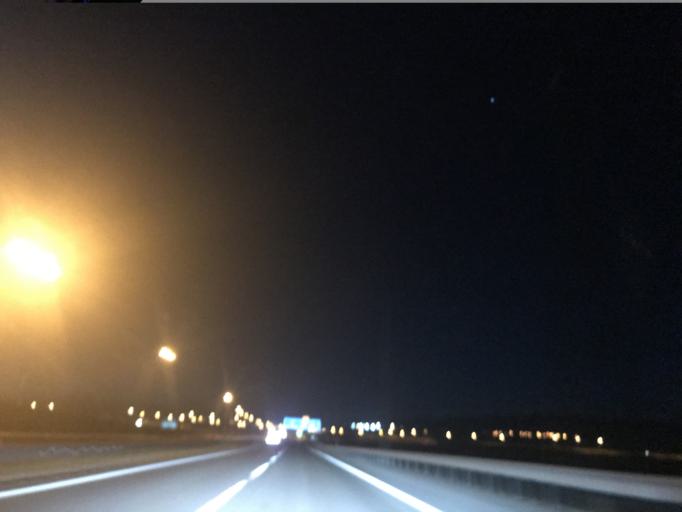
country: TR
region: Nigde
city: Ulukisla
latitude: 37.6501
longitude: 34.3506
